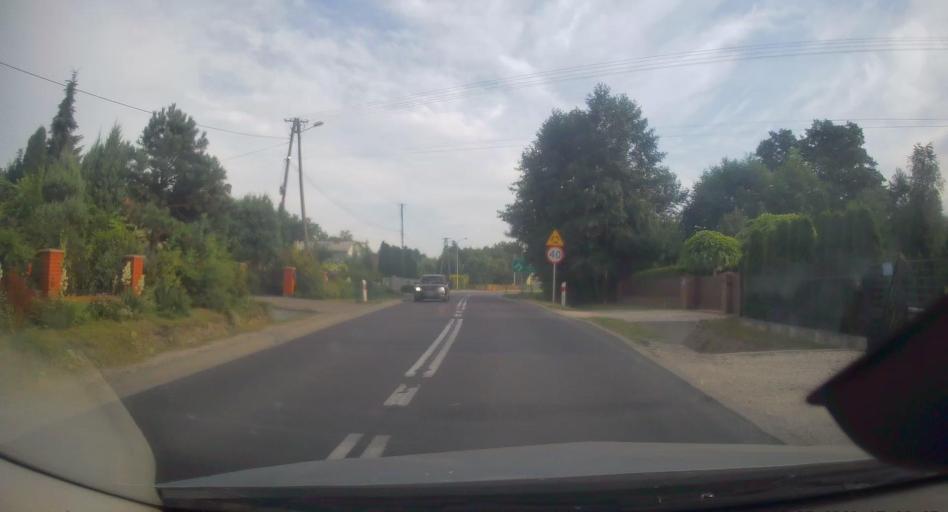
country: PL
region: Lesser Poland Voivodeship
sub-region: Powiat brzeski
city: Przyborow
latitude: 50.0243
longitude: 20.6334
